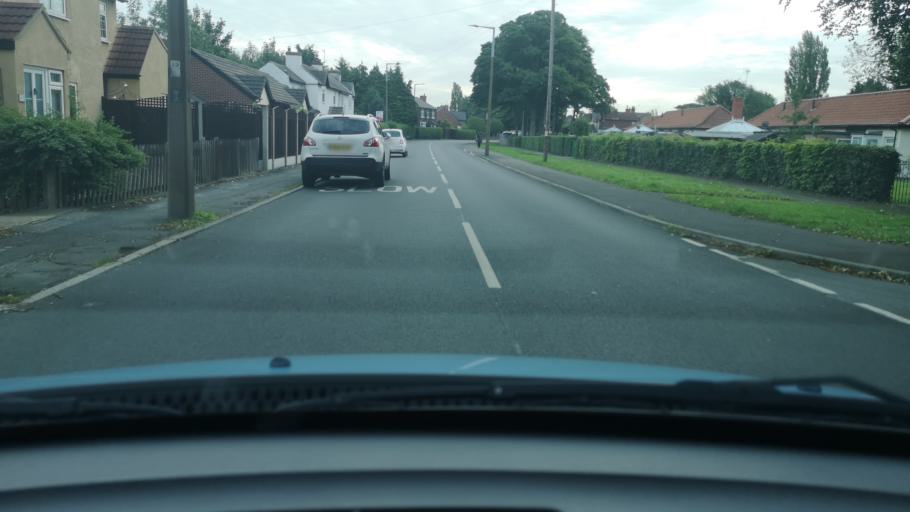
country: GB
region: England
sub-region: North Lincolnshire
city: Scunthorpe
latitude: 53.5845
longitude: -0.6603
